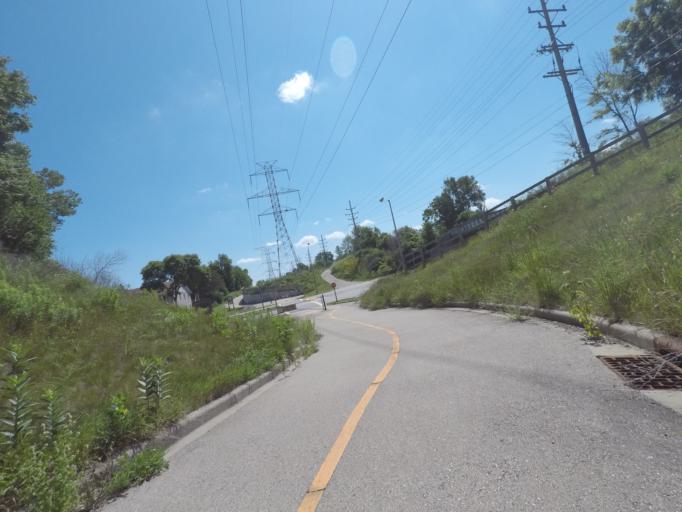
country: US
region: Wisconsin
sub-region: Waukesha County
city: Elm Grove
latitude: 43.0104
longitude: -88.0576
